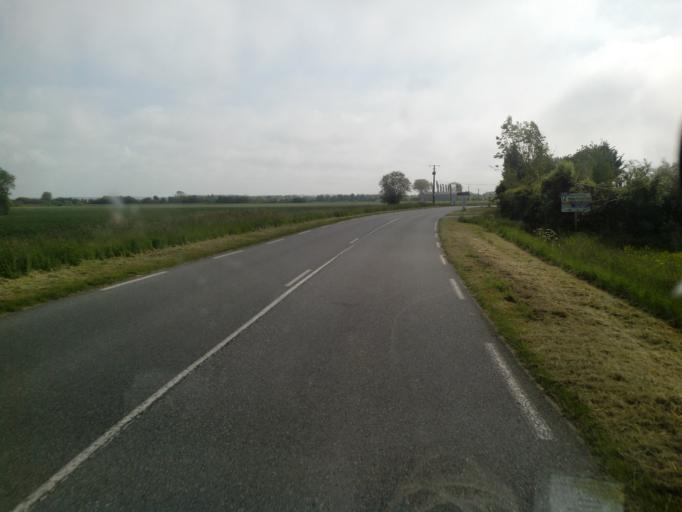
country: FR
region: Picardie
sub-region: Departement de la Somme
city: Le Crotoy
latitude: 50.2311
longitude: 1.6429
